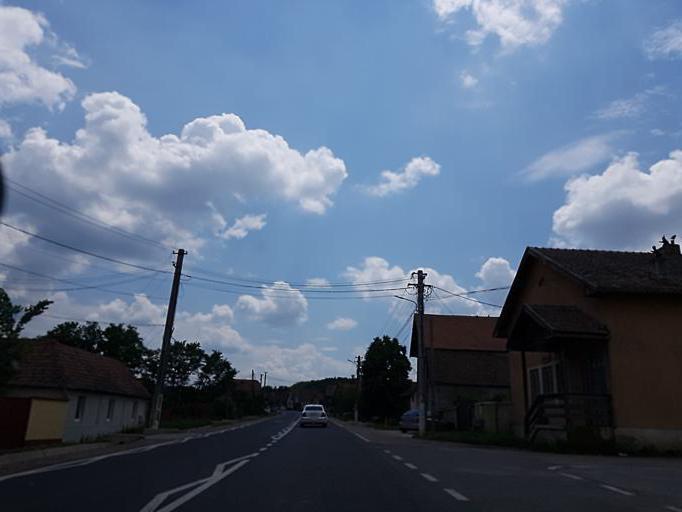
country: RO
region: Sibiu
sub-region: Comuna Slimnic
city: Slimnic
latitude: 45.9137
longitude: 24.1536
